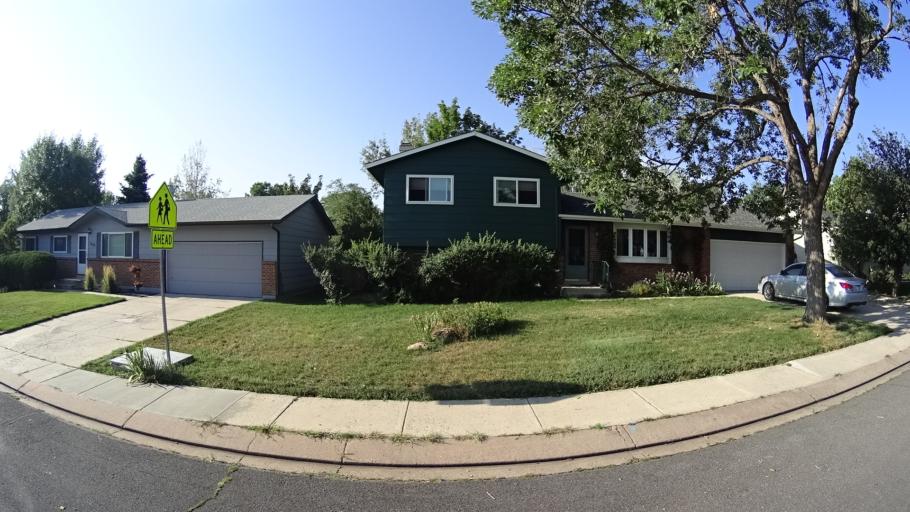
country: US
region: Colorado
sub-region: El Paso County
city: Colorado Springs
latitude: 38.8885
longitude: -104.8457
